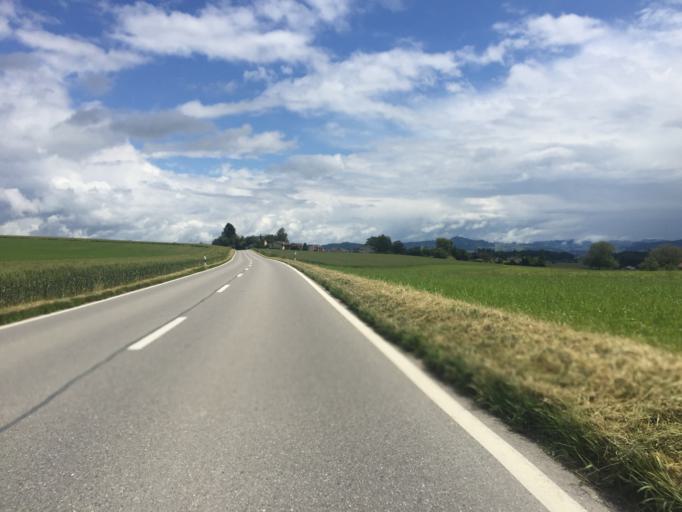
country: CH
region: Bern
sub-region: Bern-Mittelland District
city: Wohlen
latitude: 46.9828
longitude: 7.3747
